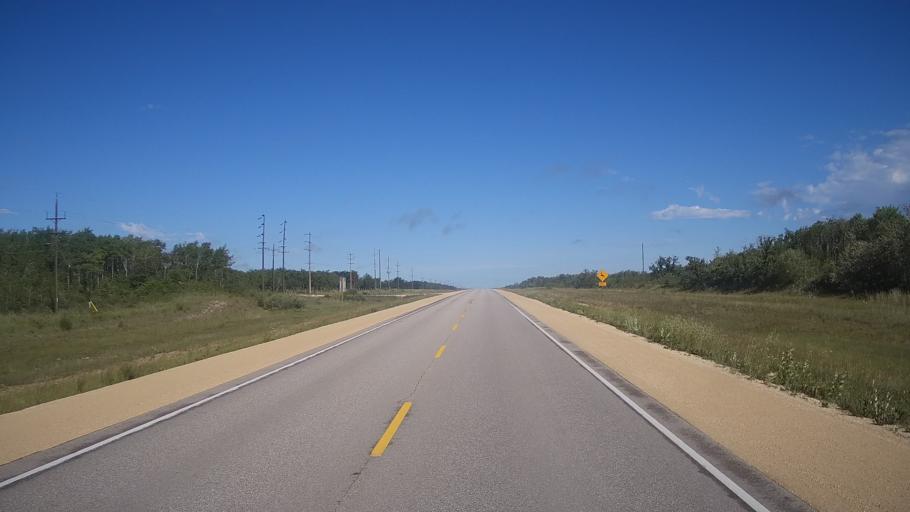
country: CA
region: Manitoba
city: Stonewall
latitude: 50.2160
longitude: -97.6759
